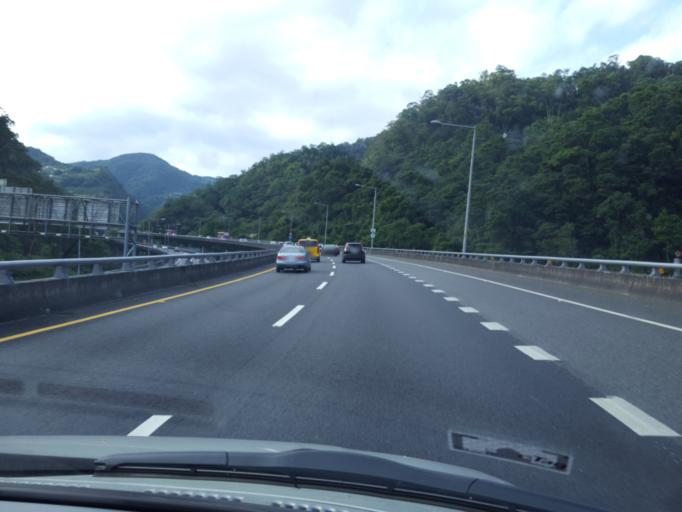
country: TW
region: Taiwan
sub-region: Keelung
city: Keelung
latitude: 24.9445
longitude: 121.7109
